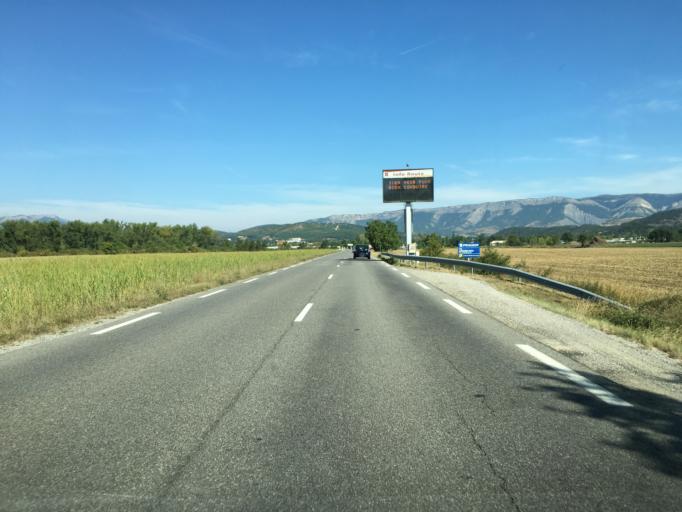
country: FR
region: Provence-Alpes-Cote d'Azur
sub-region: Departement des Hautes-Alpes
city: Laragne-Monteglin
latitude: 44.2953
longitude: 5.8412
